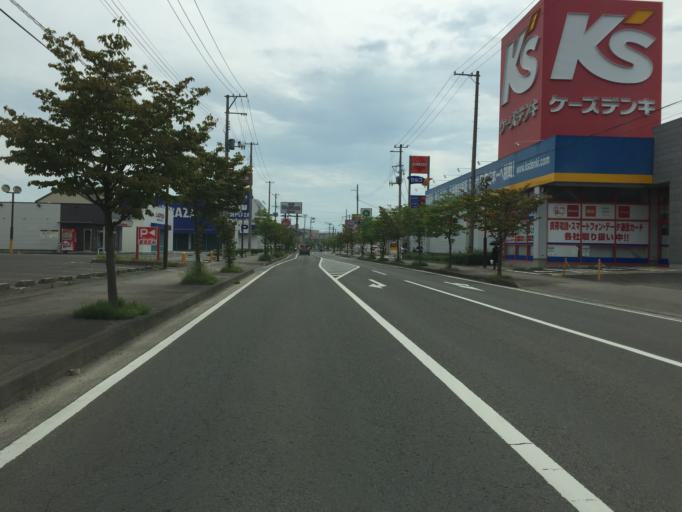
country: JP
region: Fukushima
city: Fukushima-shi
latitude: 37.7891
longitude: 140.4506
